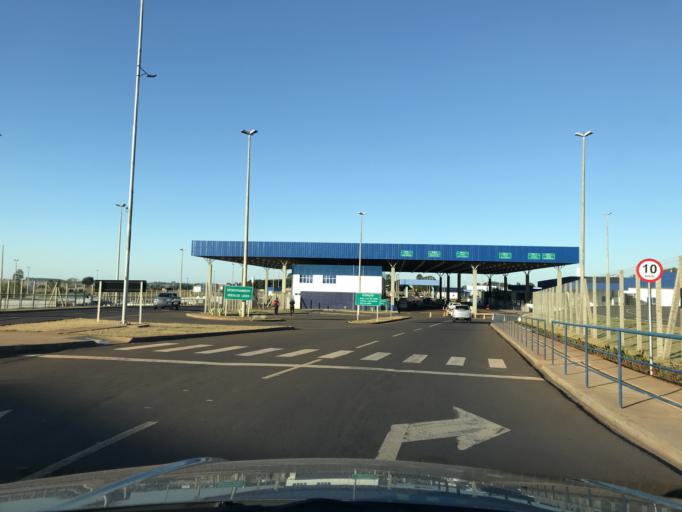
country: PY
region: Canindeyu
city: Salto del Guaira
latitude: -24.0034
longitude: -54.3213
